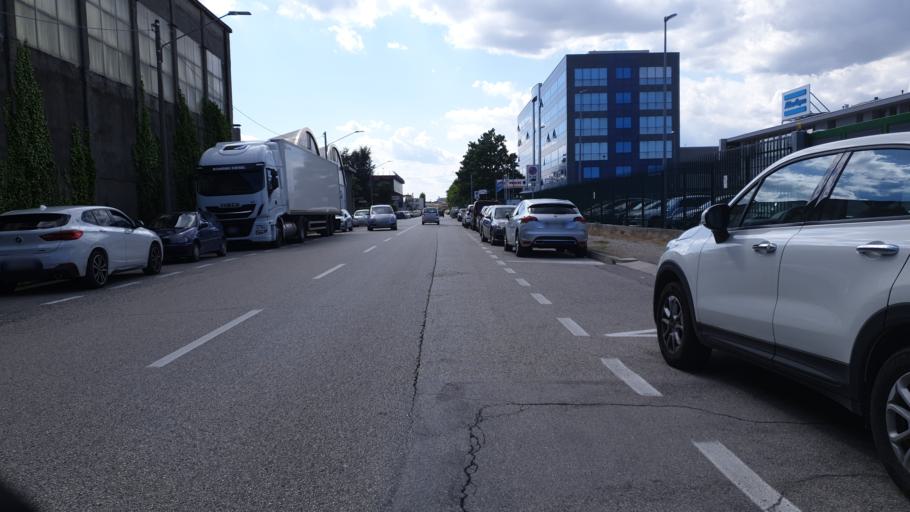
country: IT
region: Veneto
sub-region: Provincia di Padova
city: Noventa
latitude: 45.4127
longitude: 11.9257
